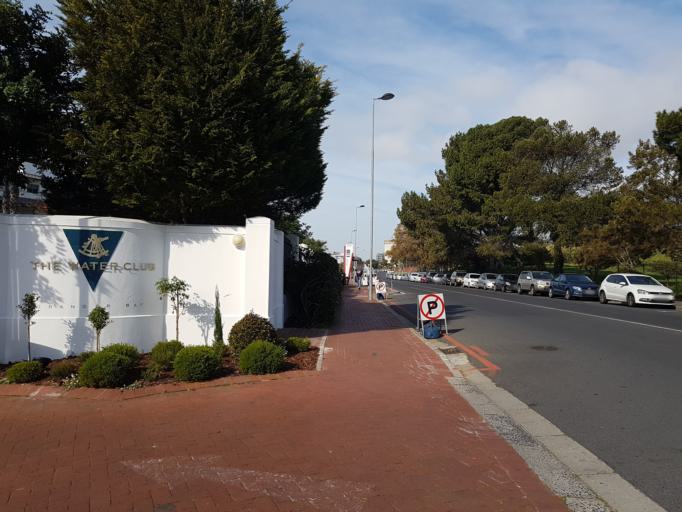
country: ZA
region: Western Cape
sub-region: City of Cape Town
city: Cape Town
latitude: -33.9010
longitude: 18.4126
